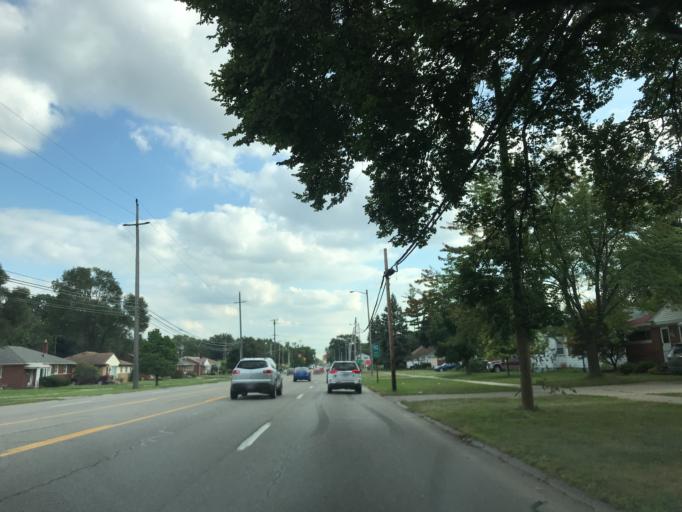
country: US
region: Michigan
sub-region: Wayne County
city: Redford
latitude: 42.3877
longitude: -83.2956
